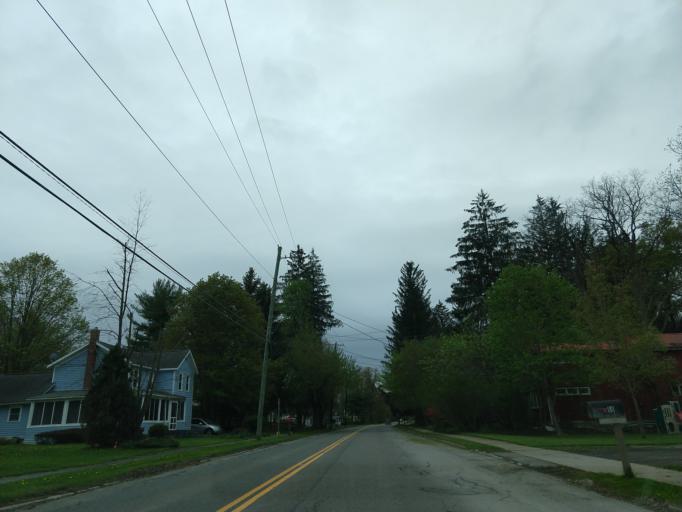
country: US
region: New York
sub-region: Tompkins County
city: Dryden
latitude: 42.5116
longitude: -76.3513
